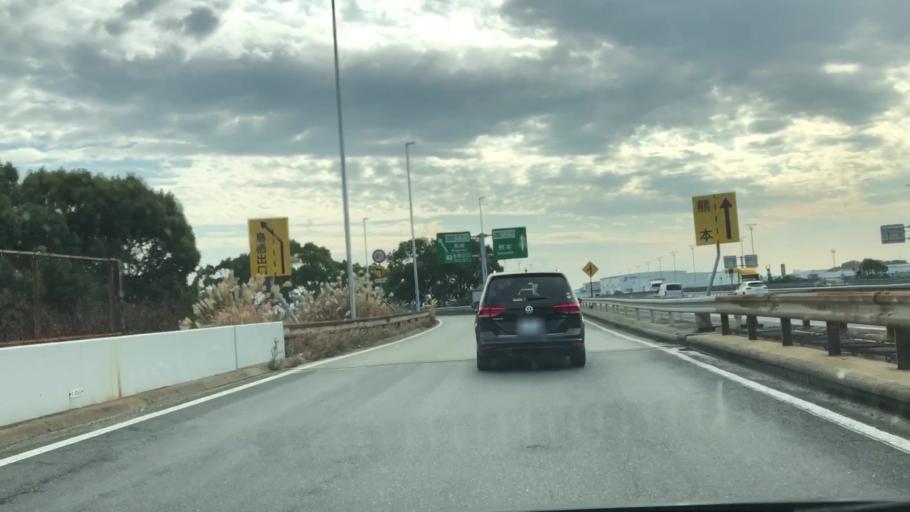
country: JP
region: Saga Prefecture
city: Tosu
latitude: 33.3964
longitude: 130.5386
